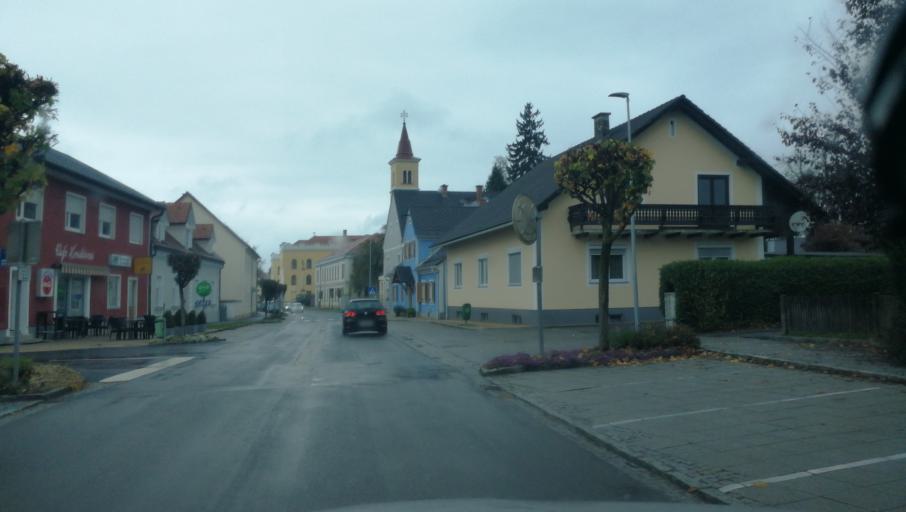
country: AT
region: Styria
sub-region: Politischer Bezirk Leibnitz
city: Strass in Steiermark
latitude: 46.7262
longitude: 15.6287
